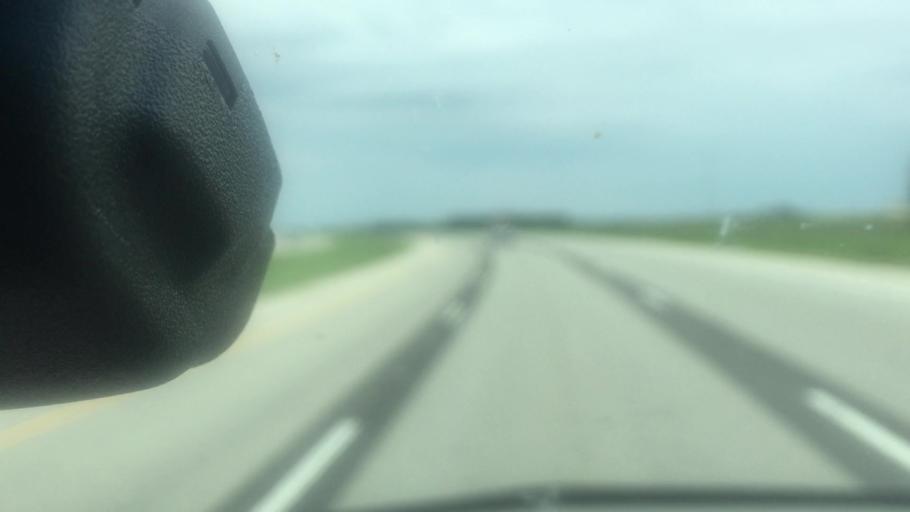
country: US
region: Illinois
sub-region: Sangamon County
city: Williamsville
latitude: 40.0207
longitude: -89.4963
